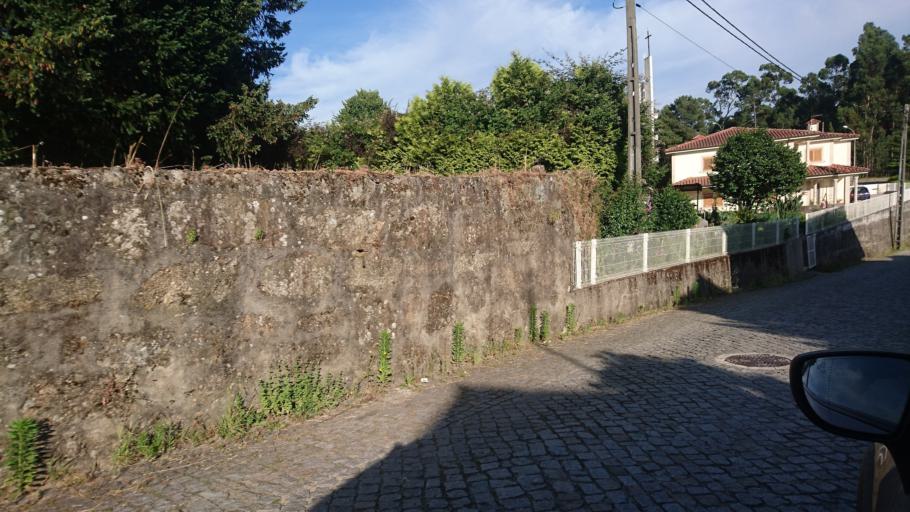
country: PT
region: Porto
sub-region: Paredes
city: Recarei
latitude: 41.1270
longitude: -8.3686
